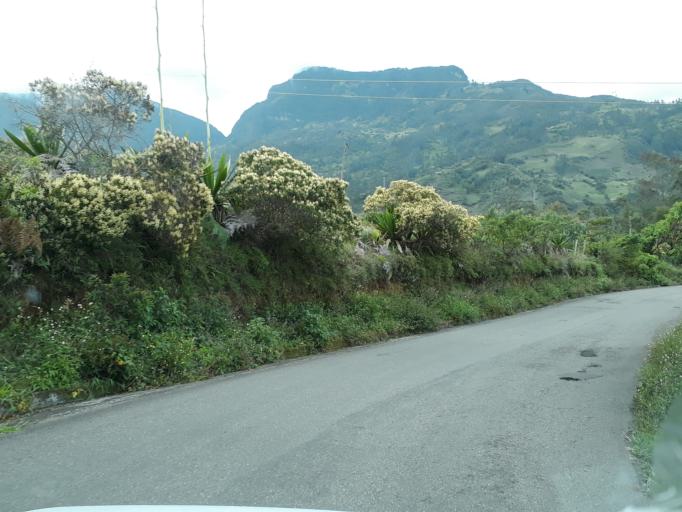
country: CO
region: Cundinamarca
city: Junin
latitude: 4.8144
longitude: -73.6762
